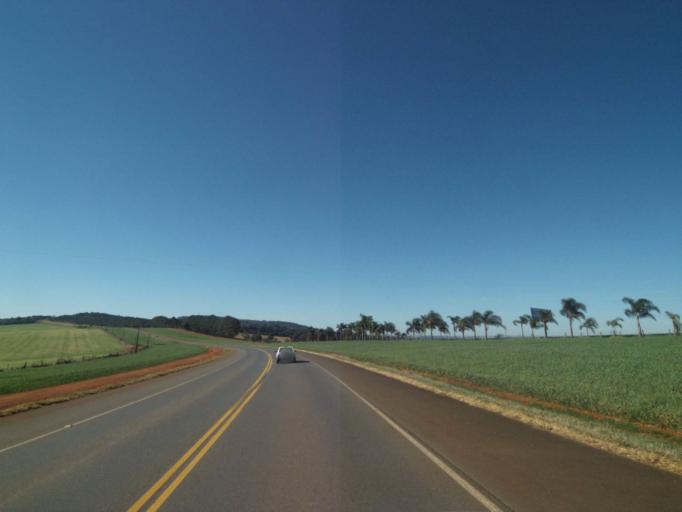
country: BR
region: Parana
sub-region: Tibagi
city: Tibagi
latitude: -24.4233
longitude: -50.3755
